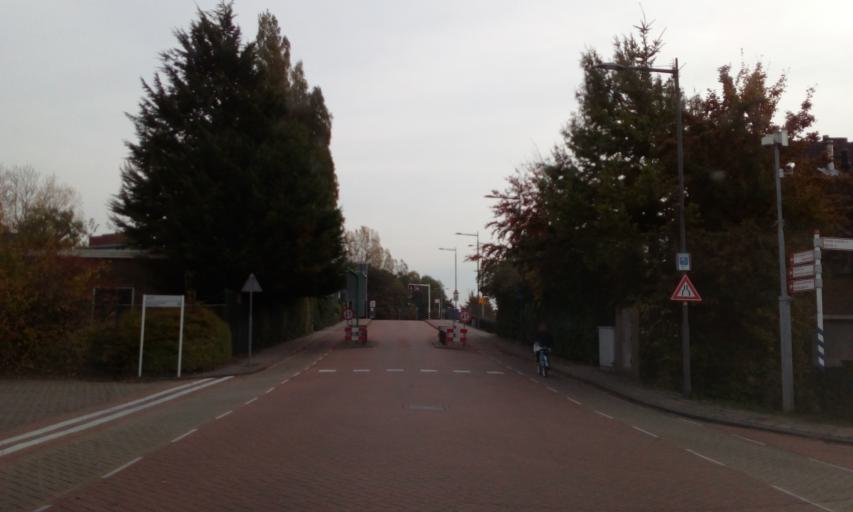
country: NL
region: South Holland
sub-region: Gemeente Lansingerland
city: Berkel en Rodenrijs
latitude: 51.9773
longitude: 4.4577
